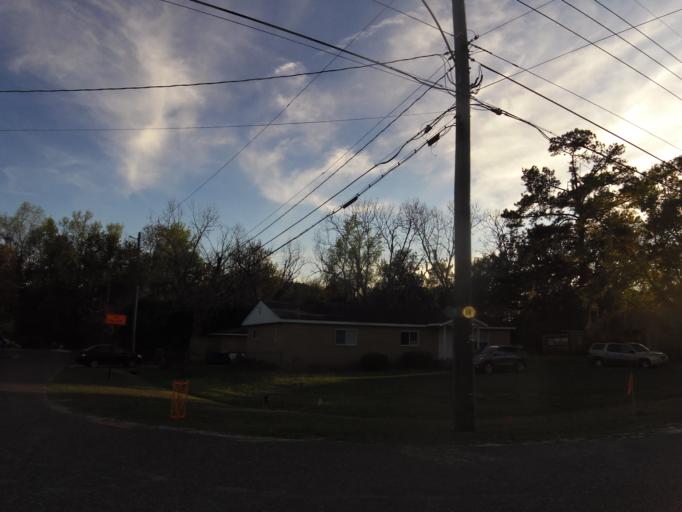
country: US
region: Florida
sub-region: Duval County
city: Jacksonville
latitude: 30.4685
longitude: -81.6495
